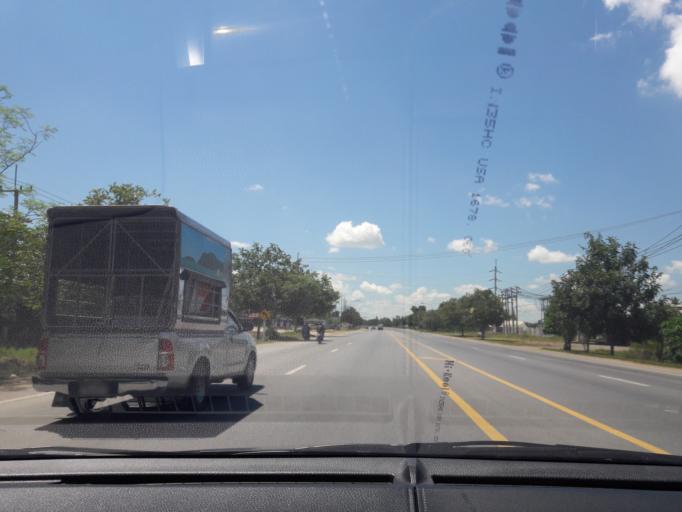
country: TH
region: Kanchanaburi
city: Tha Maka
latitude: 14.0340
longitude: 99.8206
